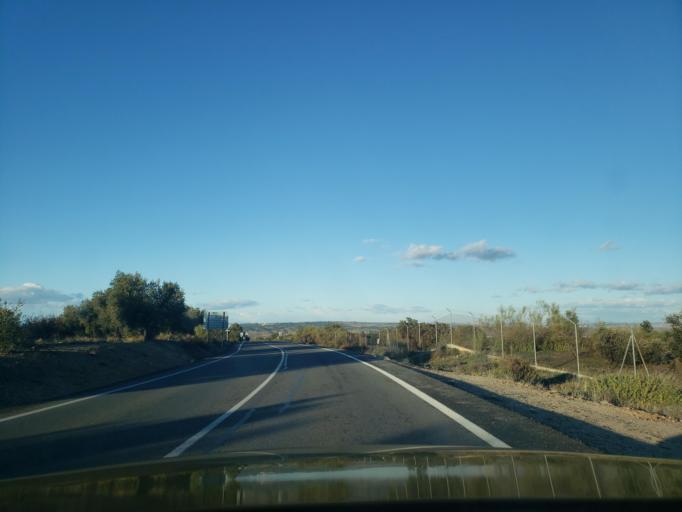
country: ES
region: Castille-La Mancha
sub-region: Province of Toledo
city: Toledo
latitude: 39.8370
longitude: -4.0194
